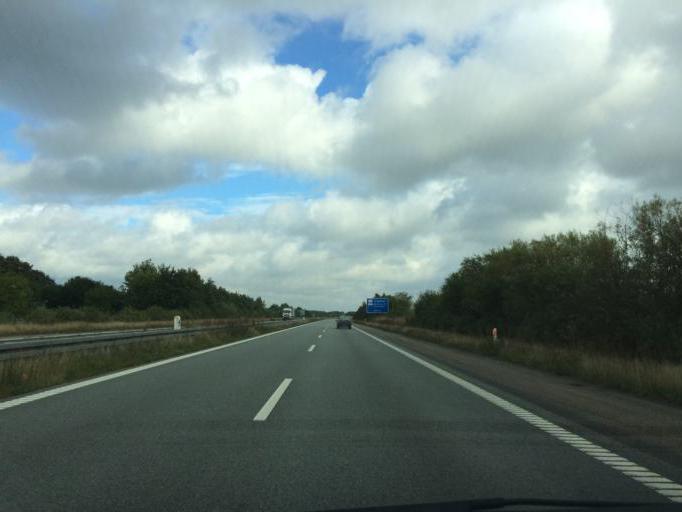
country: DK
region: North Denmark
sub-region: Alborg Kommune
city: Vodskov
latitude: 57.1271
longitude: 10.0748
